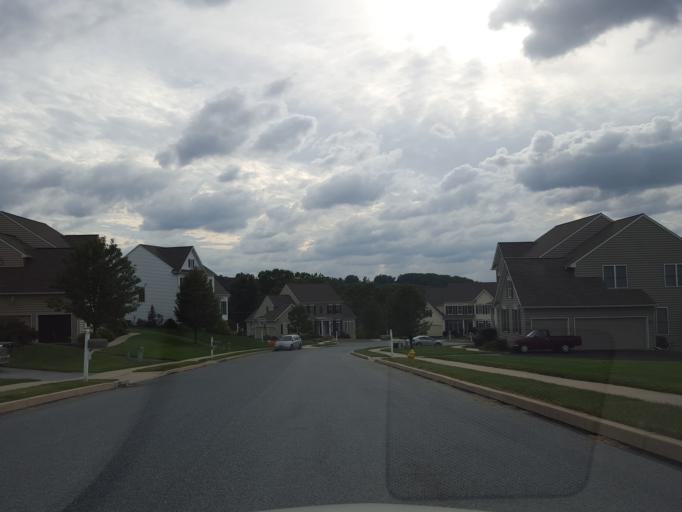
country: US
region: Pennsylvania
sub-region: York County
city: Yoe
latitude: 39.9318
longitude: -76.6519
